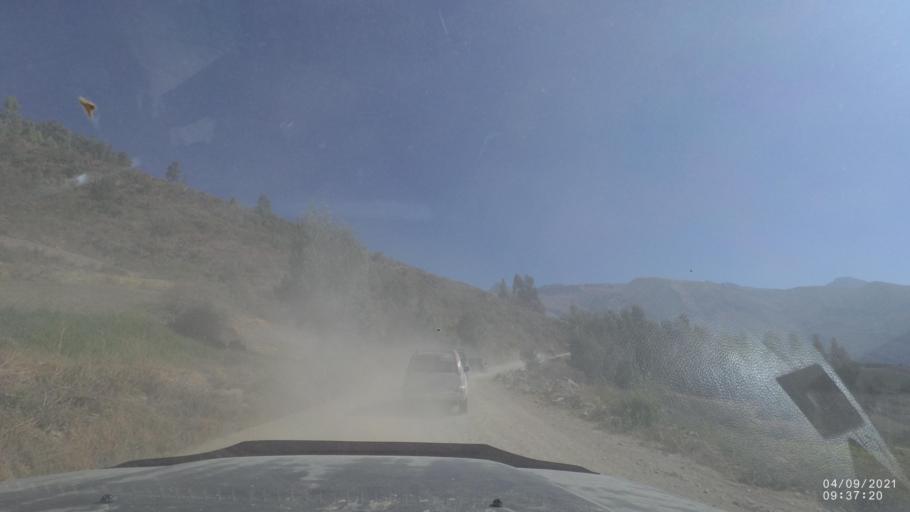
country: BO
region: Cochabamba
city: Sipe Sipe
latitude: -17.3482
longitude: -66.3829
